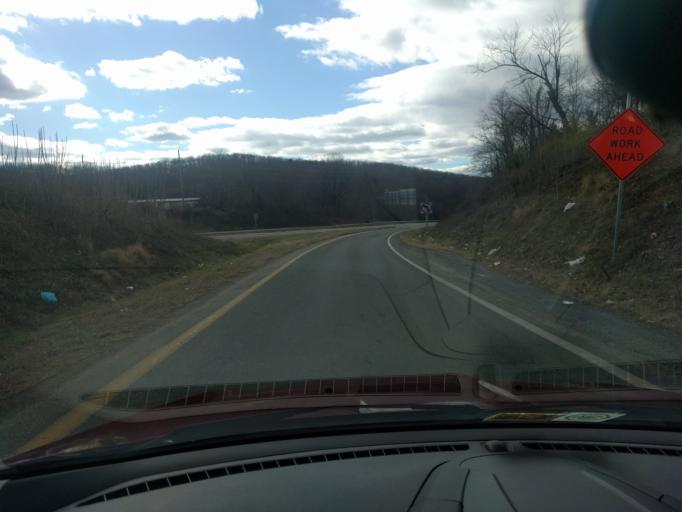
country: US
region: Virginia
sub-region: City of Lynchburg
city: Lynchburg
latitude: 37.3785
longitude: -79.1319
